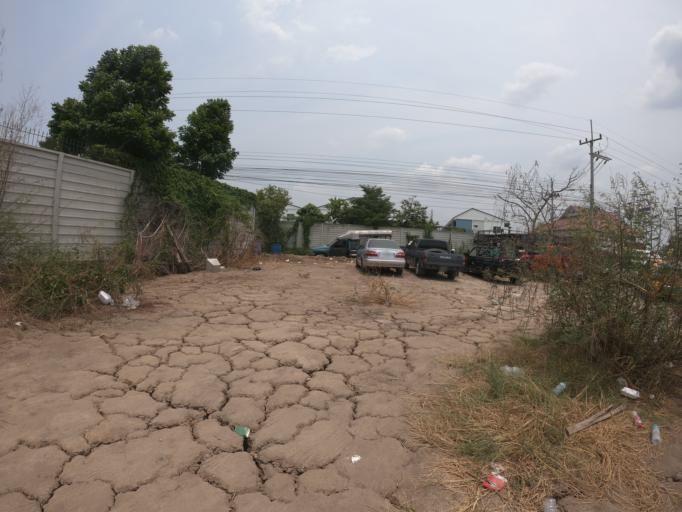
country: TH
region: Phra Nakhon Si Ayutthaya
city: Ban Bang Kadi Pathum Thani
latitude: 14.0082
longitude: 100.5686
